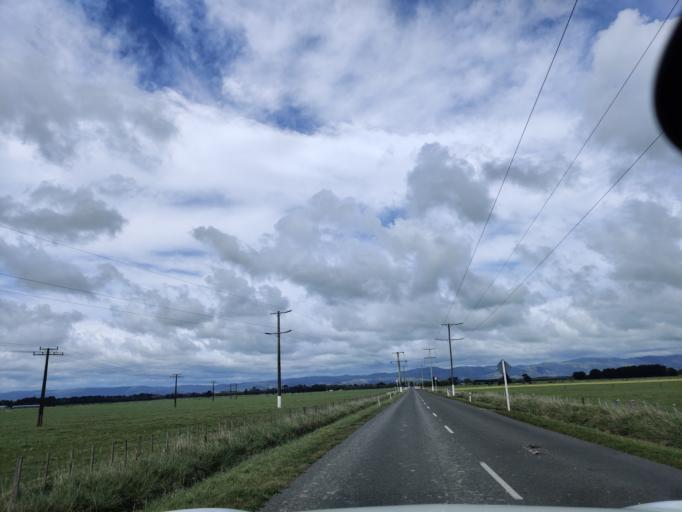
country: NZ
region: Manawatu-Wanganui
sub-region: Palmerston North City
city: Palmerston North
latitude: -40.3490
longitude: 175.5333
